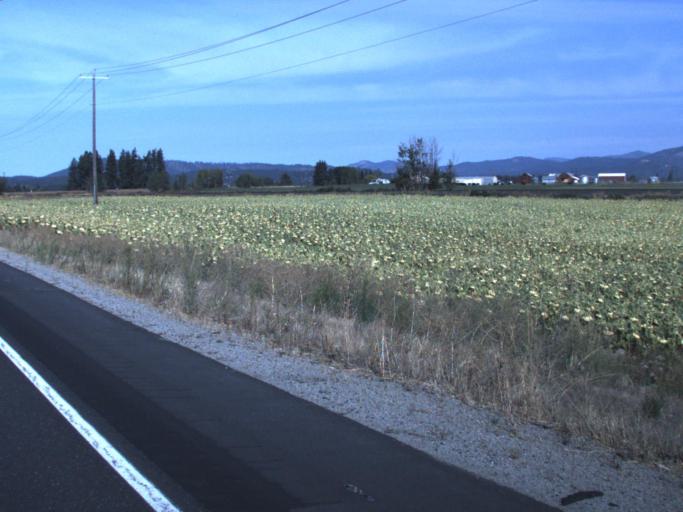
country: US
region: Washington
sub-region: Spokane County
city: Deer Park
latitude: 47.9687
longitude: -117.5091
